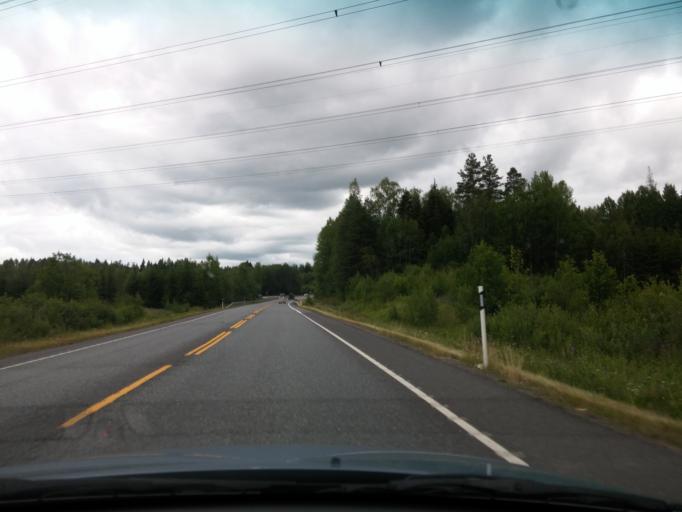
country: FI
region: Uusimaa
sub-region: Porvoo
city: Porvoo
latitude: 60.4285
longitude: 25.5778
